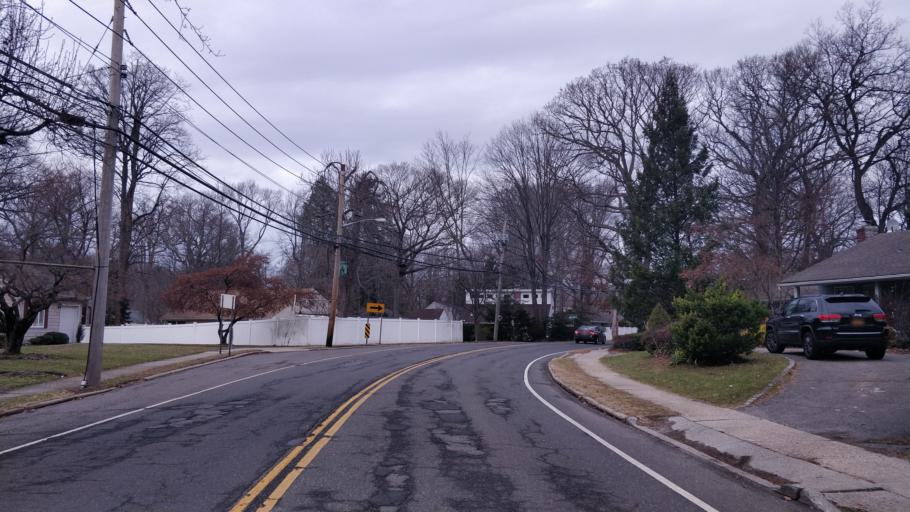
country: US
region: New York
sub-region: Nassau County
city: Glen Cove
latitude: 40.8762
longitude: -73.6306
